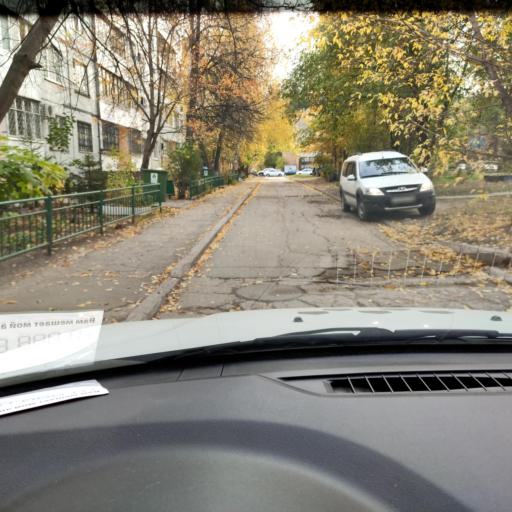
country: RU
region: Samara
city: Tol'yatti
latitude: 53.5087
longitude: 49.4327
